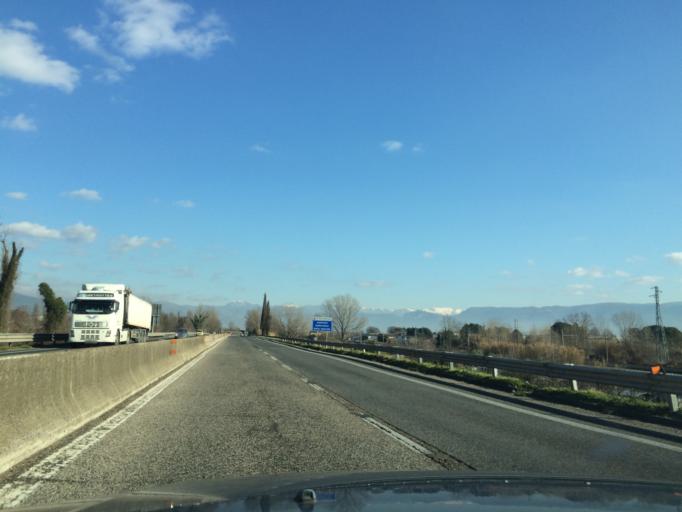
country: IT
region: Umbria
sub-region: Provincia di Terni
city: Terni
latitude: 42.5694
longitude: 12.5880
